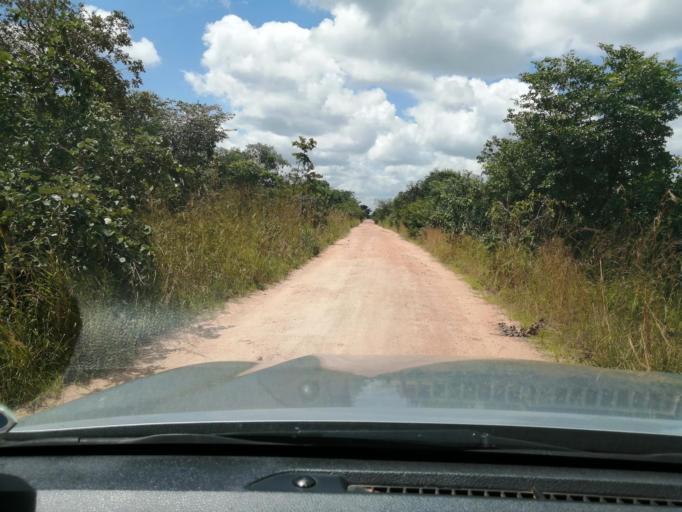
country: ZM
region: Lusaka
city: Lusaka
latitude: -15.1469
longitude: 27.9318
